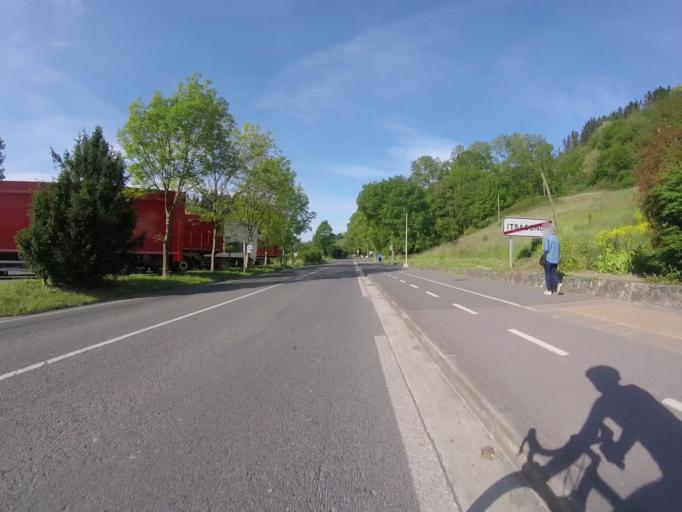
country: ES
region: Basque Country
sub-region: Provincia de Guipuzcoa
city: Arama
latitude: 43.0658
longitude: -2.1666
